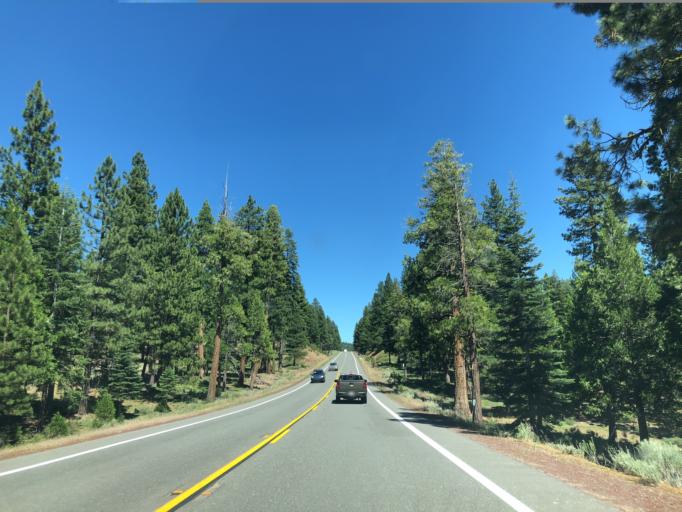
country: US
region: California
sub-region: Lassen County
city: Susanville
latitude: 40.4393
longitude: -120.8502
